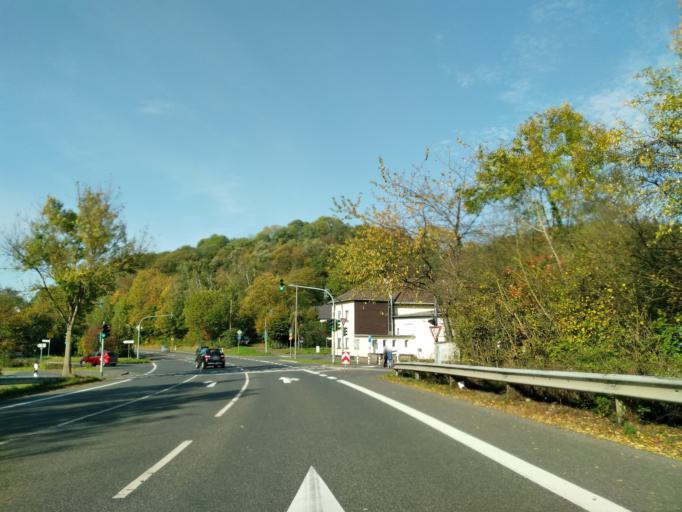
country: DE
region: North Rhine-Westphalia
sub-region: Regierungsbezirk Koln
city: Hennef
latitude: 50.7046
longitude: 7.2886
